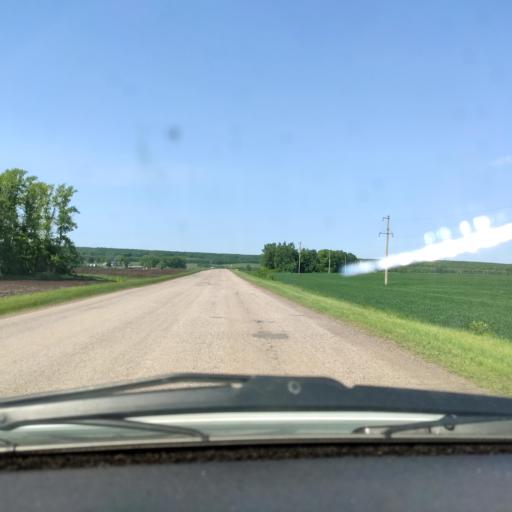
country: RU
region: Bashkortostan
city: Chishmy
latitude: 54.4683
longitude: 55.5412
